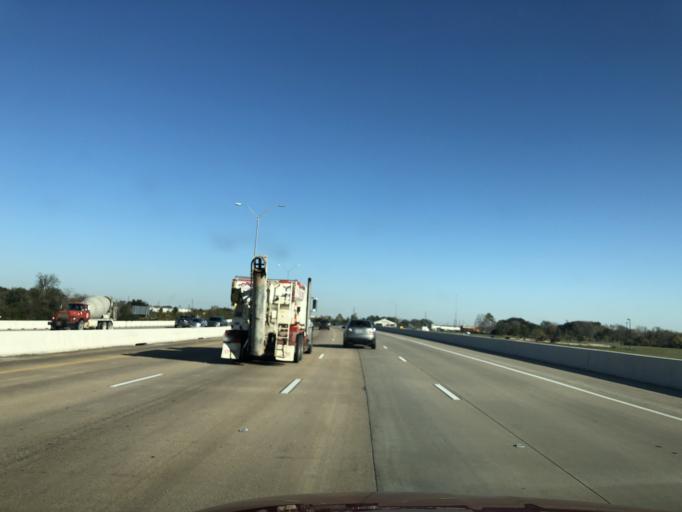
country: US
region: Texas
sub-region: Fort Bend County
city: Fresno
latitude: 29.5962
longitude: -95.4352
